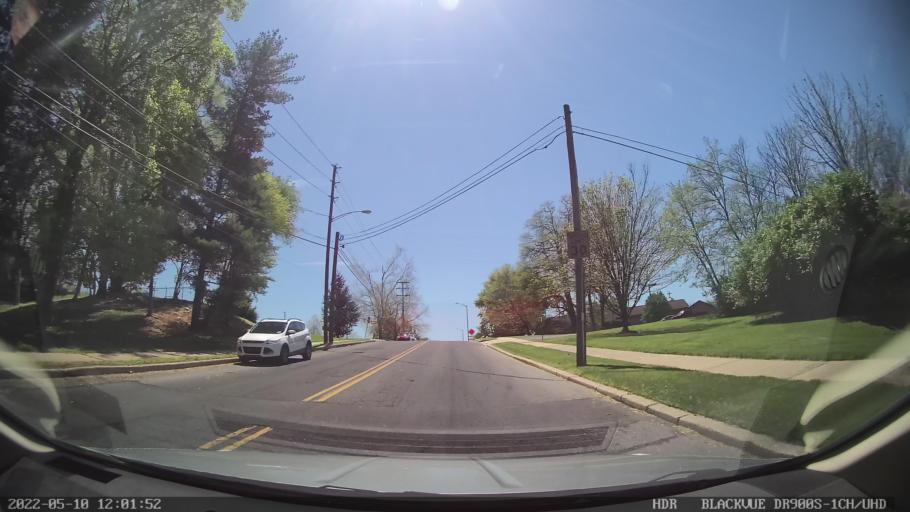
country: US
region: Pennsylvania
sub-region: Berks County
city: West Reading
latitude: 40.3244
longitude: -75.9482
